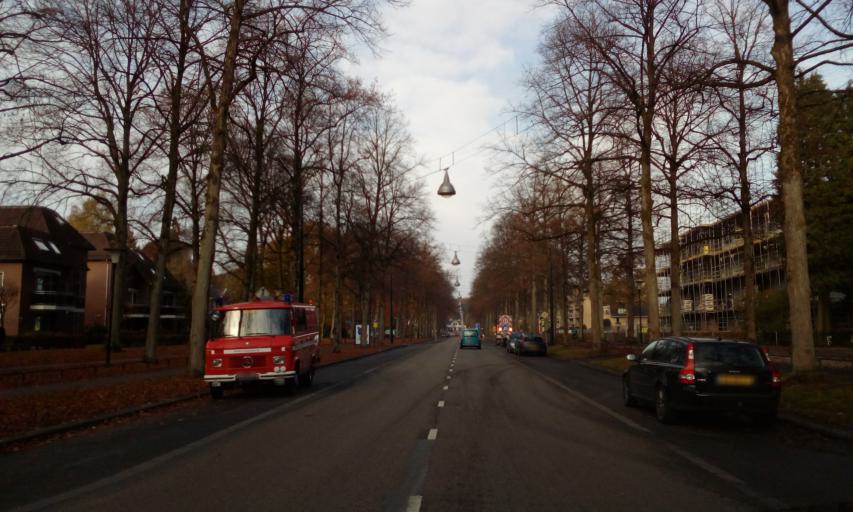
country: NL
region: Gelderland
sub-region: Gemeente Apeldoorn
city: Apeldoorn
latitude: 52.2241
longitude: 5.9508
